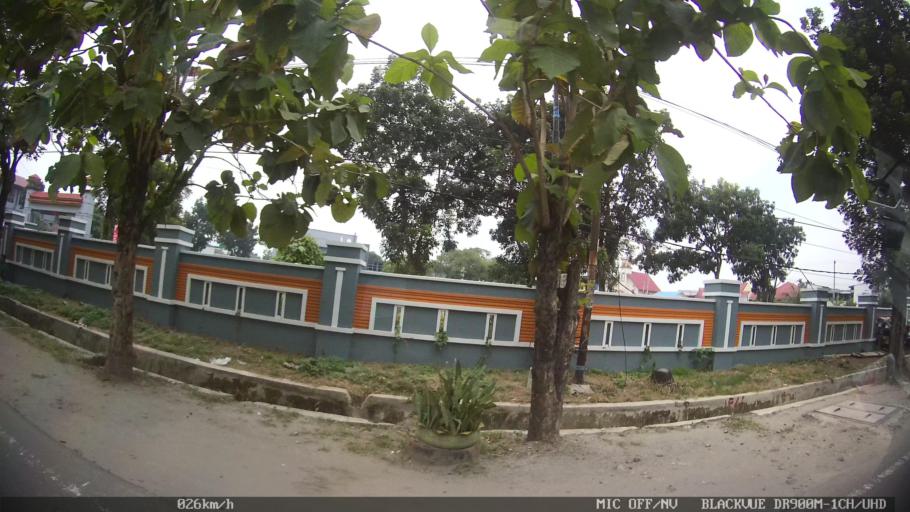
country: ID
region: North Sumatra
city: Medan
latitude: 3.5601
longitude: 98.7198
